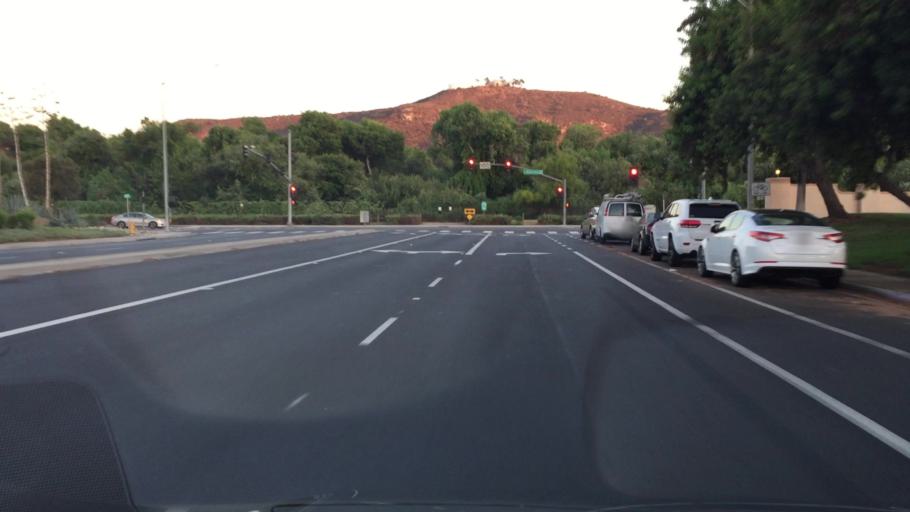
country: US
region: California
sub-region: San Diego County
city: Rancho San Diego
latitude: 32.7437
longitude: -116.9348
